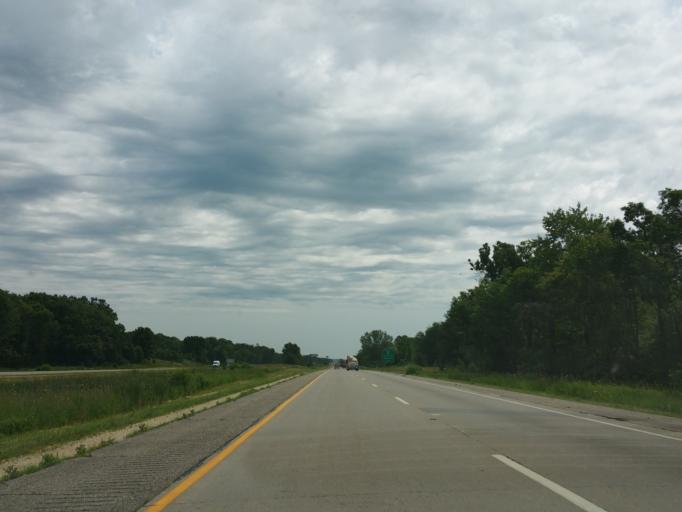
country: US
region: Wisconsin
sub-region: Juneau County
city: Mauston
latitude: 43.7319
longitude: -89.9184
